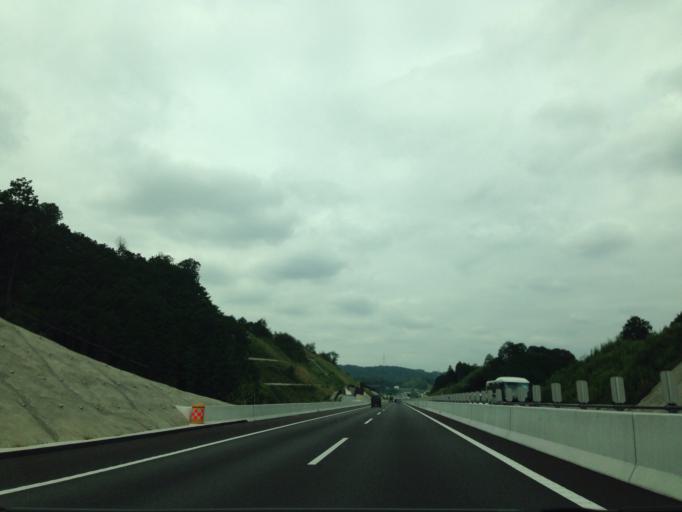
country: JP
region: Aichi
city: Gamagori
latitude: 34.9093
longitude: 137.2953
